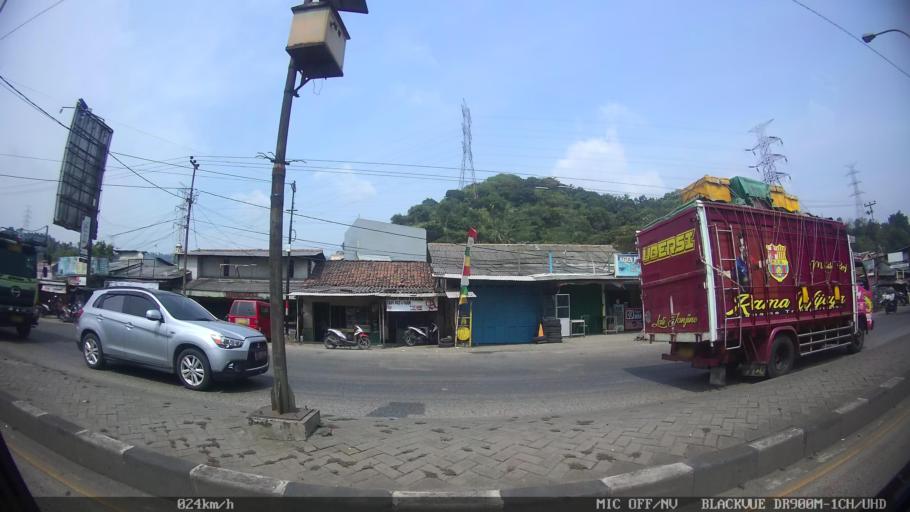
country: ID
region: Banten
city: Kubangkepuh
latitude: -5.9366
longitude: 106.0022
